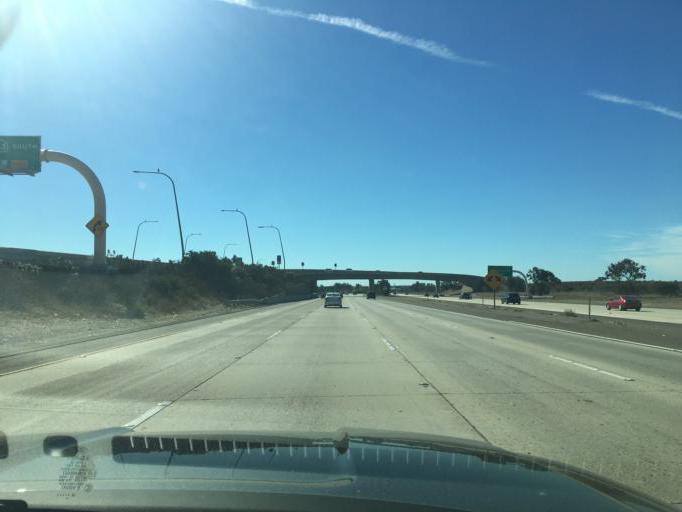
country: US
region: California
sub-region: San Diego County
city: Poway
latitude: 32.8643
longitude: -117.1104
